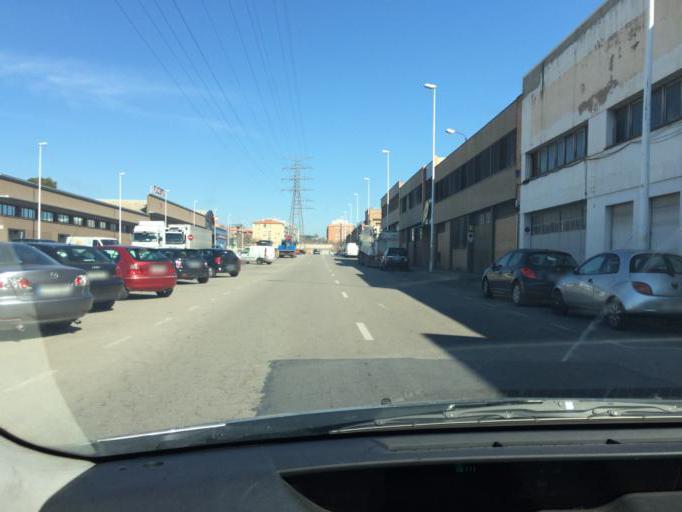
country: ES
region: Catalonia
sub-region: Provincia de Barcelona
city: Manresa
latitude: 41.7340
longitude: 1.8381
